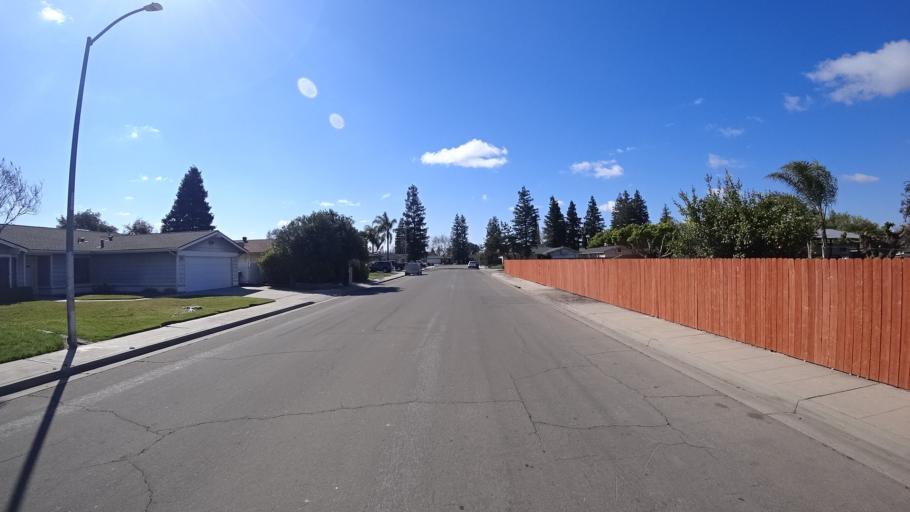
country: US
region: California
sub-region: Fresno County
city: West Park
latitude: 36.7931
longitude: -119.8840
